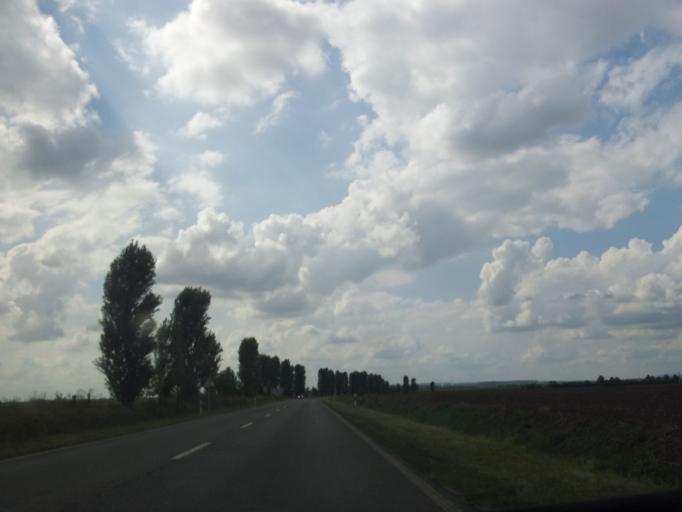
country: HU
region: Baranya
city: Mohacs
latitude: 45.9724
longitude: 18.6723
